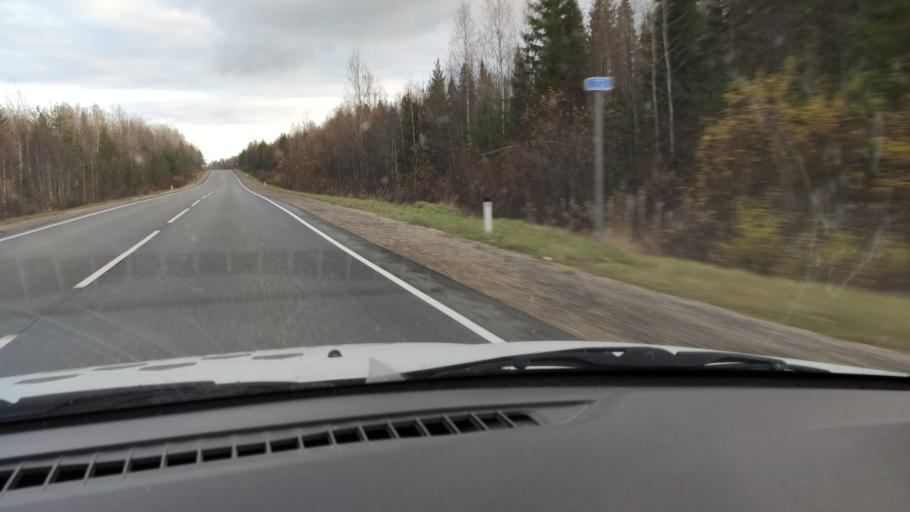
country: RU
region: Kirov
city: Omutninsk
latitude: 58.7064
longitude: 52.1035
